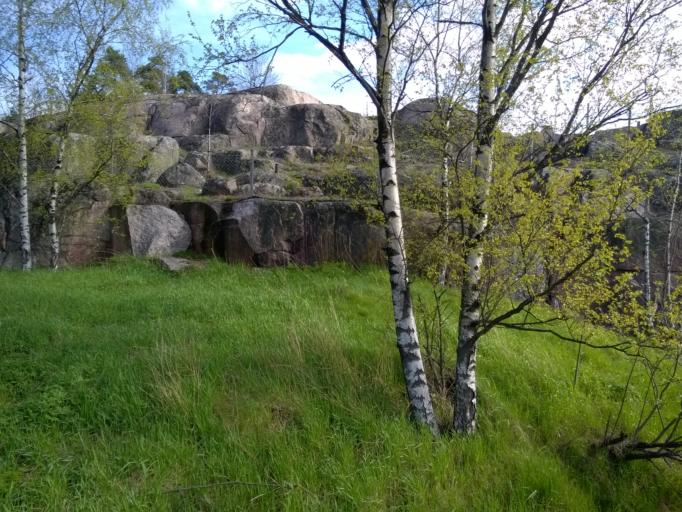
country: FI
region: Uusimaa
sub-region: Helsinki
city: Vantaa
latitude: 60.2281
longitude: 25.0020
